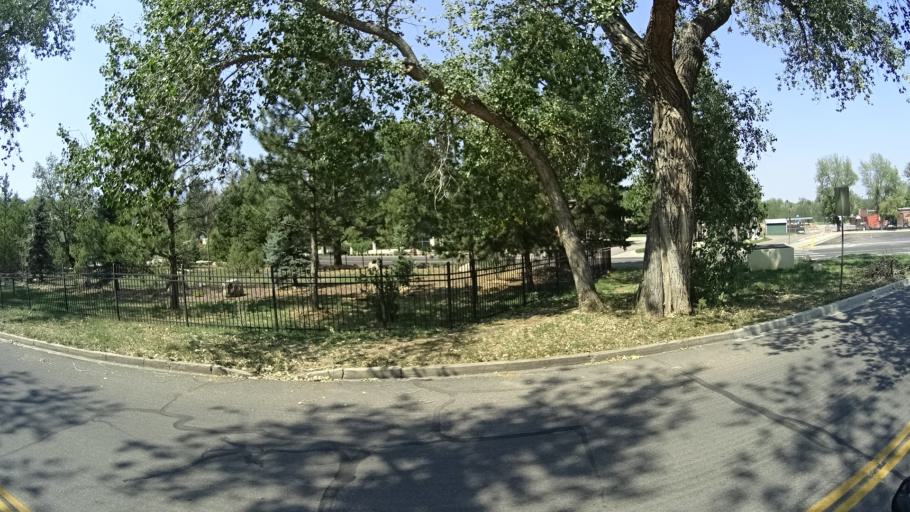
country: US
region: Colorado
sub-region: El Paso County
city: Colorado Springs
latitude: 38.7882
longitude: -104.8367
